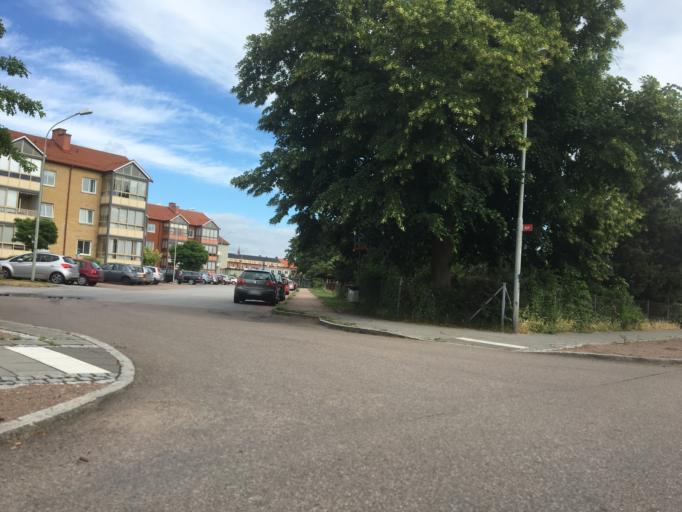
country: SE
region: Skane
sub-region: Landskrona
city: Landskrona
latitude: 55.8805
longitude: 12.8289
